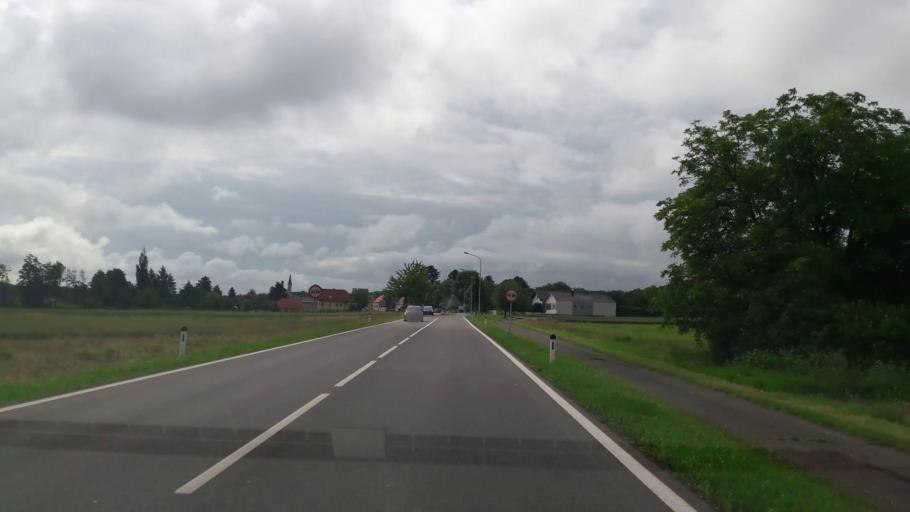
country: AT
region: Burgenland
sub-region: Politischer Bezirk Oberpullendorf
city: Oberpullendorf
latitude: 47.4795
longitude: 16.5321
